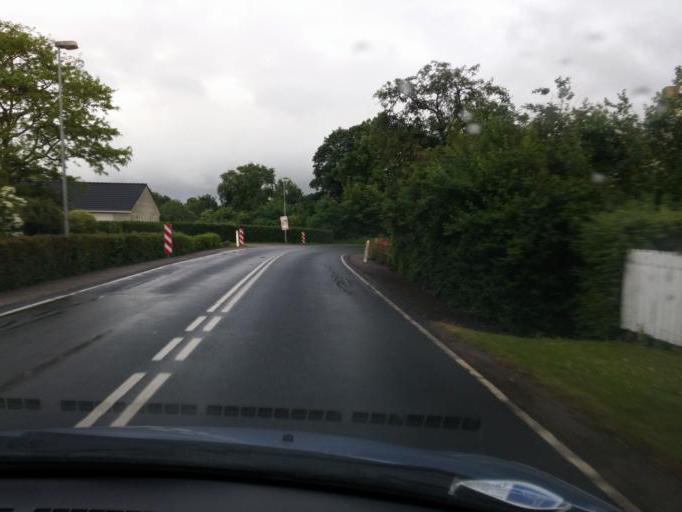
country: DK
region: South Denmark
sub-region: Kerteminde Kommune
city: Kerteminde
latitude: 55.5037
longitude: 10.6499
